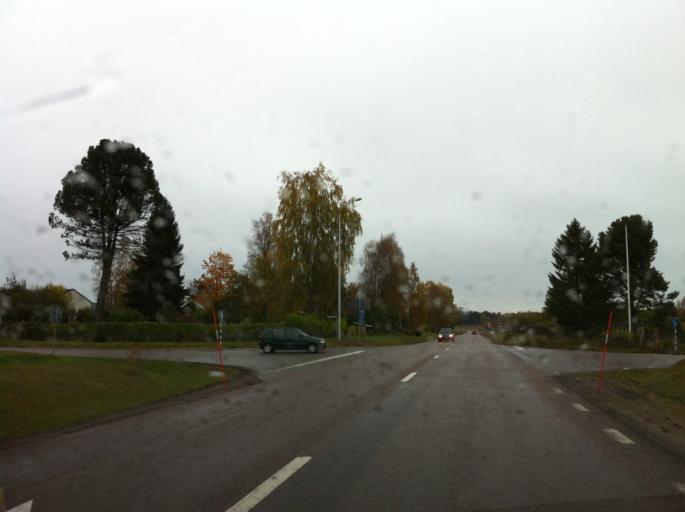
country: SE
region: Dalarna
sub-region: Ludvika Kommun
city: Grangesberg
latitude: 60.2507
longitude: 14.9795
